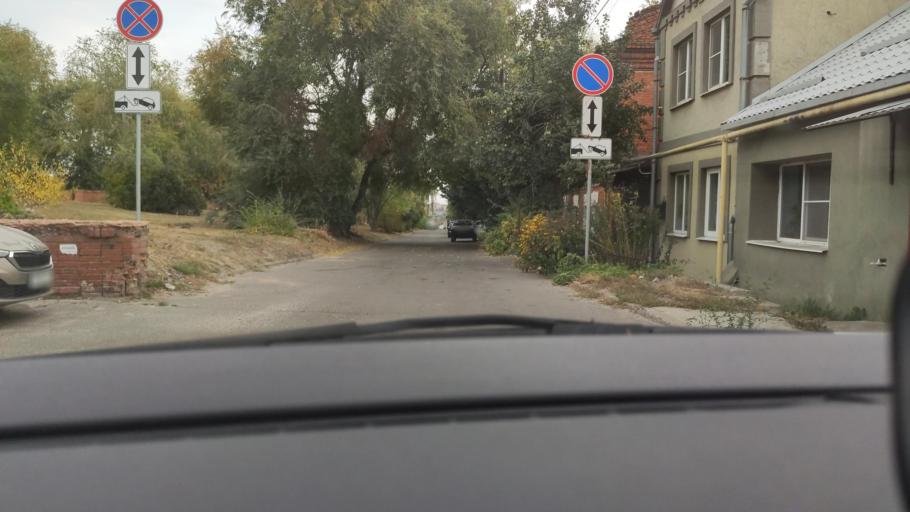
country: RU
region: Voronezj
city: Voronezh
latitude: 51.6639
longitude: 39.2154
